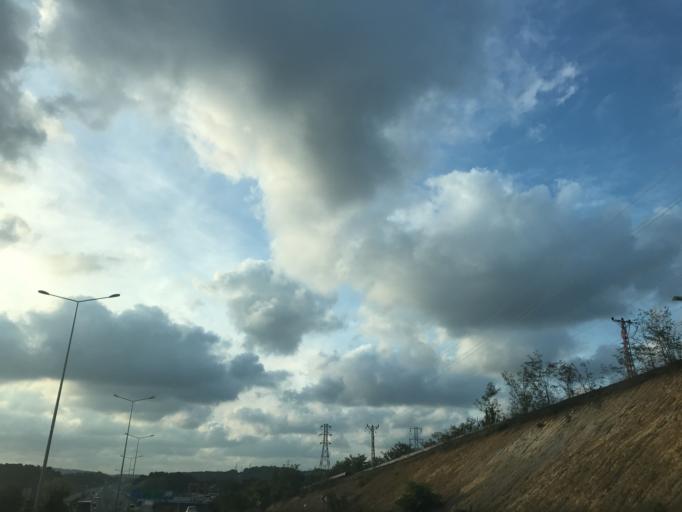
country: TR
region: Istanbul
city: Kemerburgaz
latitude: 41.1985
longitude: 28.8657
